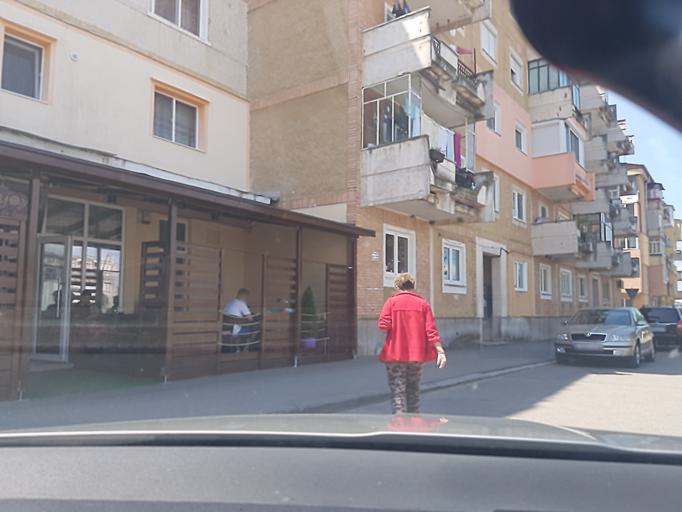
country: RO
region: Hunedoara
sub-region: Comuna Calan
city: Calan
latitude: 45.7328
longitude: 23.0253
